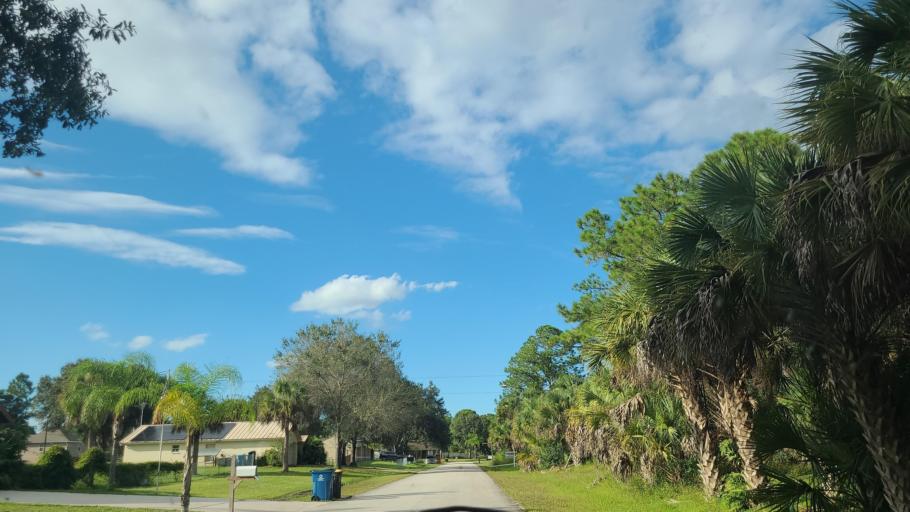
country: US
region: Florida
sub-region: Brevard County
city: June Park
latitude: 28.0009
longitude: -80.6949
